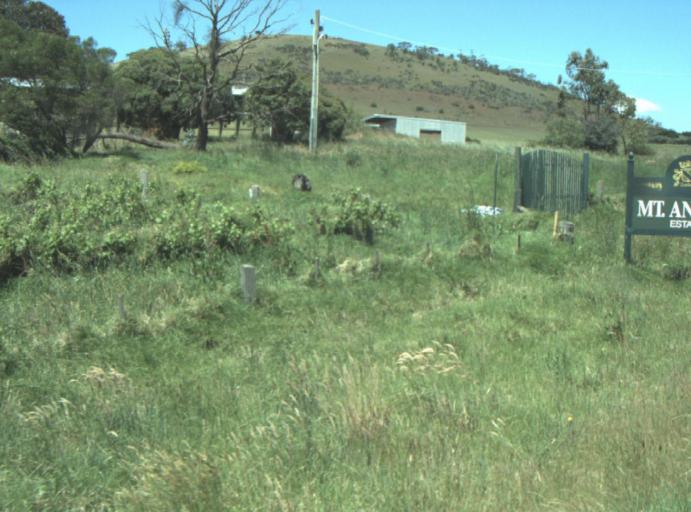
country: AU
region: Victoria
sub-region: Greater Geelong
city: Lara
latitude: -37.8762
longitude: 144.2689
